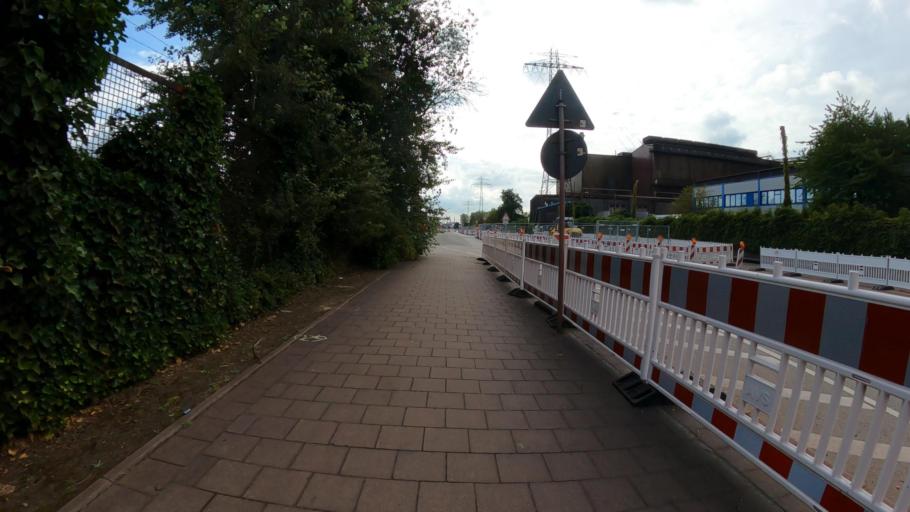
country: DE
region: Hamburg
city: Altona
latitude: 53.5254
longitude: 9.8996
